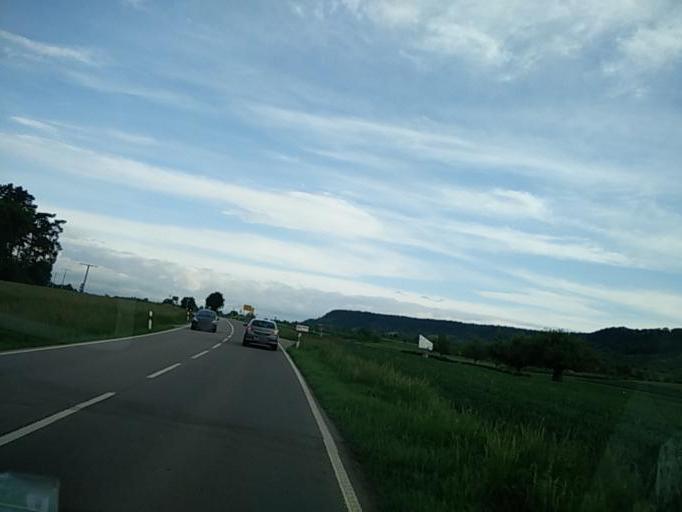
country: DE
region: Baden-Wuerttemberg
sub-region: Regierungsbezirk Stuttgart
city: Hildrizhausen
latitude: 48.5667
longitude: 8.9475
